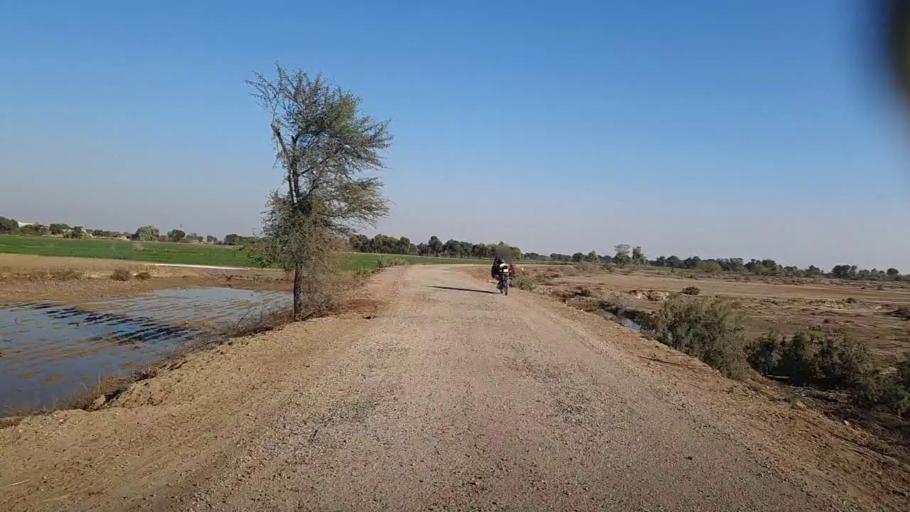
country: PK
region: Sindh
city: Khairpur
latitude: 27.8914
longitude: 69.7487
